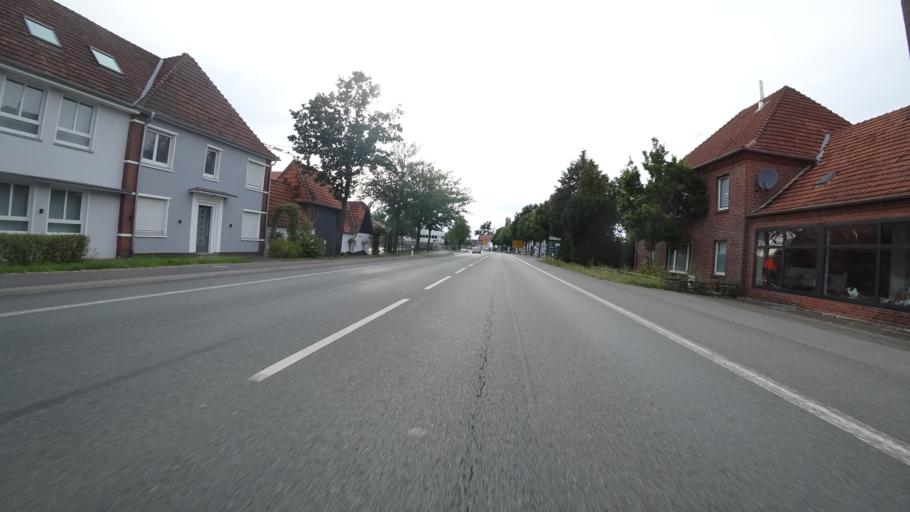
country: DE
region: North Rhine-Westphalia
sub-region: Regierungsbezirk Detmold
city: Harsewinkel
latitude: 51.9404
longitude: 8.2956
